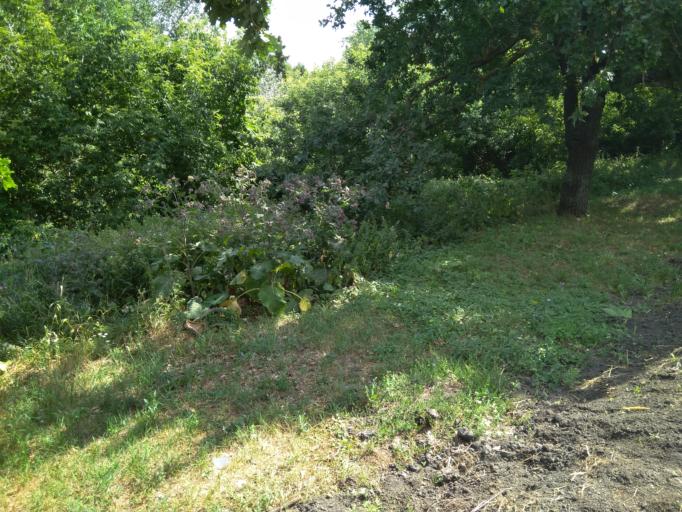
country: RU
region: Ulyanovsk
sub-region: Ulyanovskiy Rayon
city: Ulyanovsk
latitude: 54.3186
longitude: 48.4096
